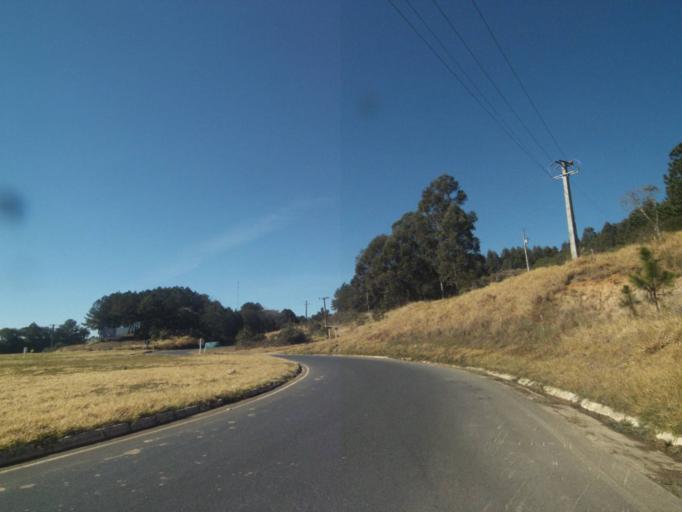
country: BR
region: Parana
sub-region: Tibagi
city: Tibagi
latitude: -24.5010
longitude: -50.4450
